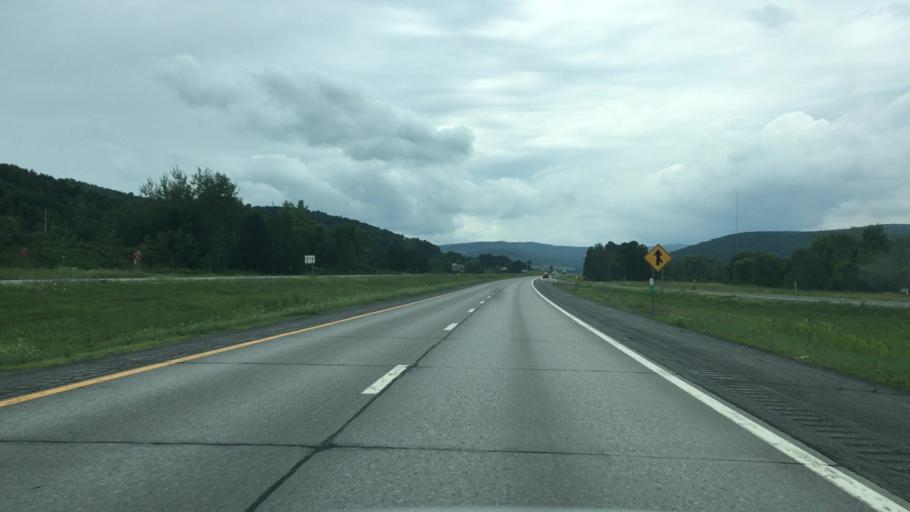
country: US
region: New York
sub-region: Schoharie County
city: Cobleskill
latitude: 42.6537
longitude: -74.5117
